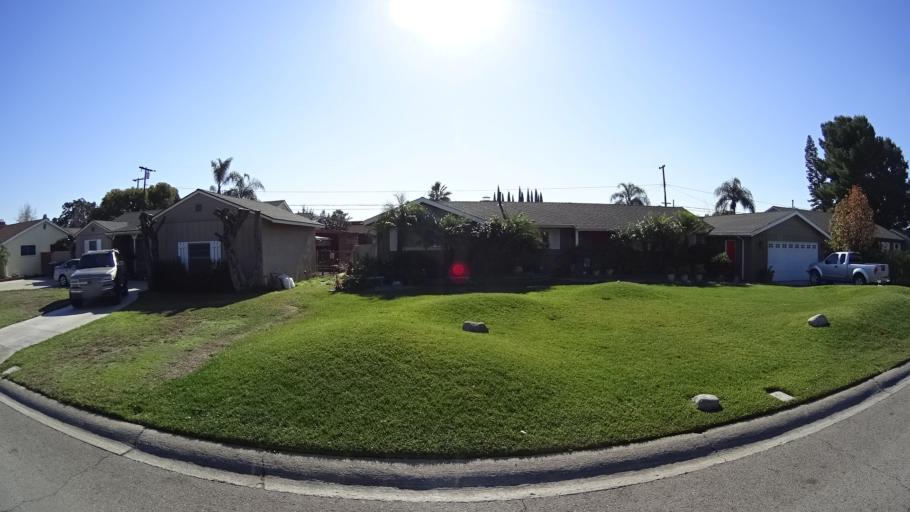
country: US
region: California
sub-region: Orange County
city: Garden Grove
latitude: 33.7876
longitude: -117.9344
